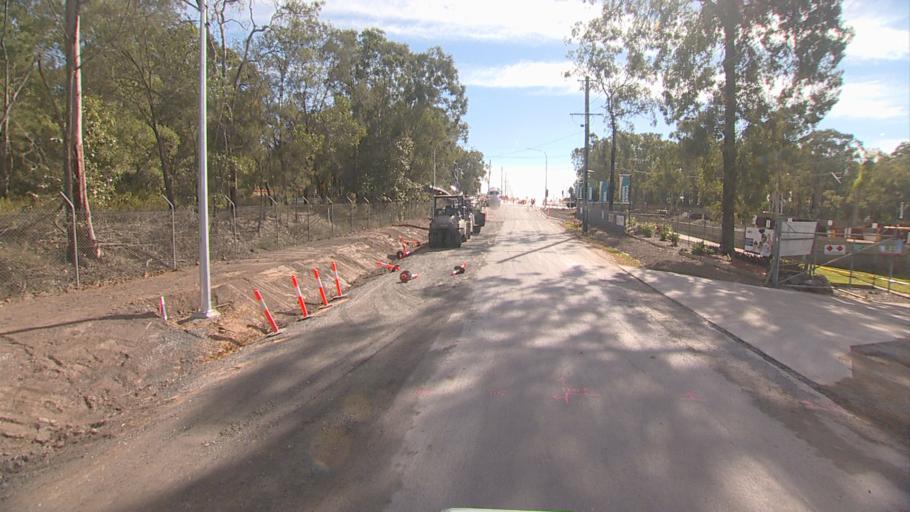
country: AU
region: Queensland
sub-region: Brisbane
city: Forest Lake
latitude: -27.6498
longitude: 152.9839
